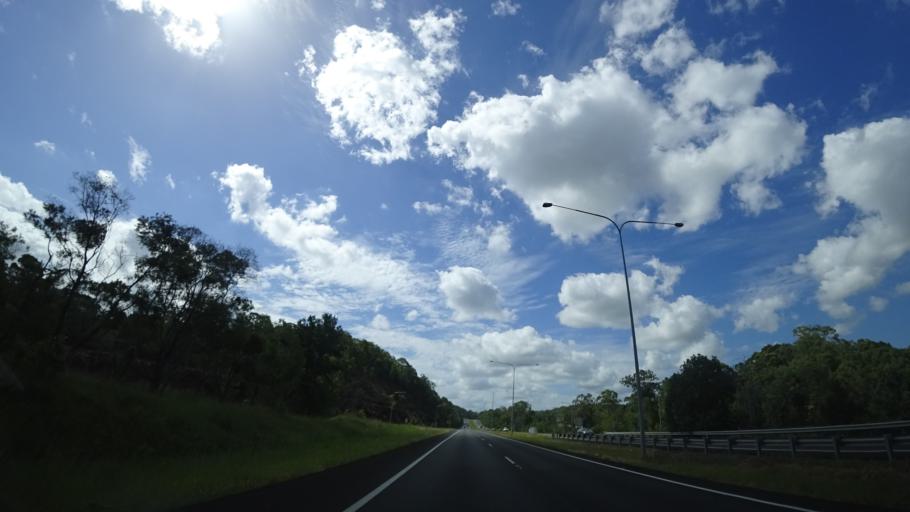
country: AU
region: Queensland
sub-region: Sunshine Coast
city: Twin Waters
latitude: -26.6152
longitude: 152.9793
